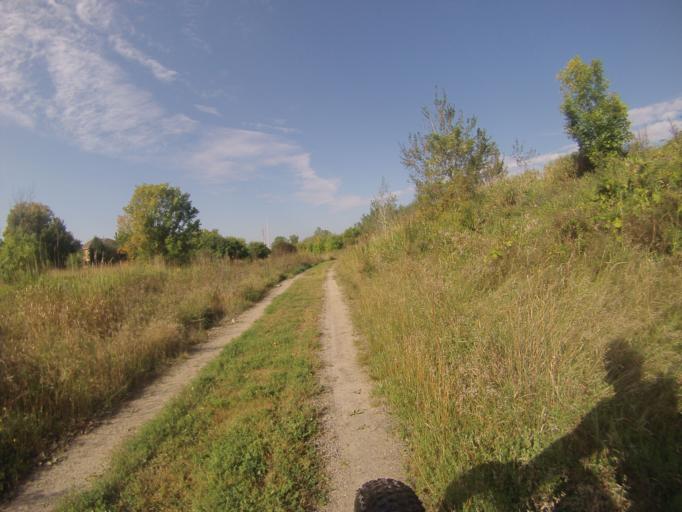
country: CA
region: Ontario
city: Ottawa
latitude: 45.3768
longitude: -75.6136
